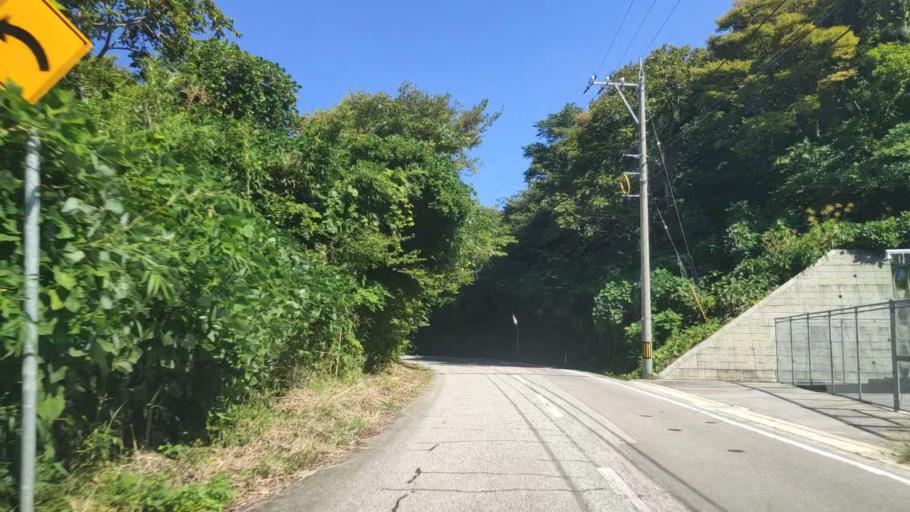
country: JP
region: Ishikawa
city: Nanao
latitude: 37.5265
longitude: 137.2676
